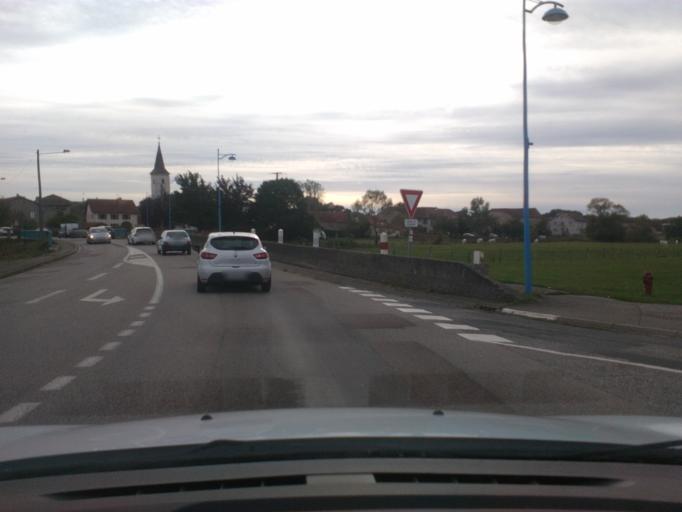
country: FR
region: Lorraine
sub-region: Departement des Vosges
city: Deyvillers
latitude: 48.2573
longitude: 6.5341
